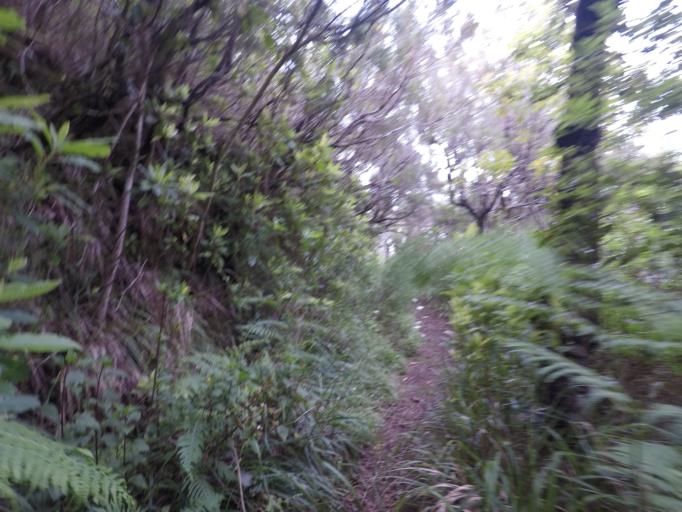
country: PT
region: Madeira
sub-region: Sao Vicente
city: Sao Vicente
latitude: 32.7690
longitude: -17.0554
